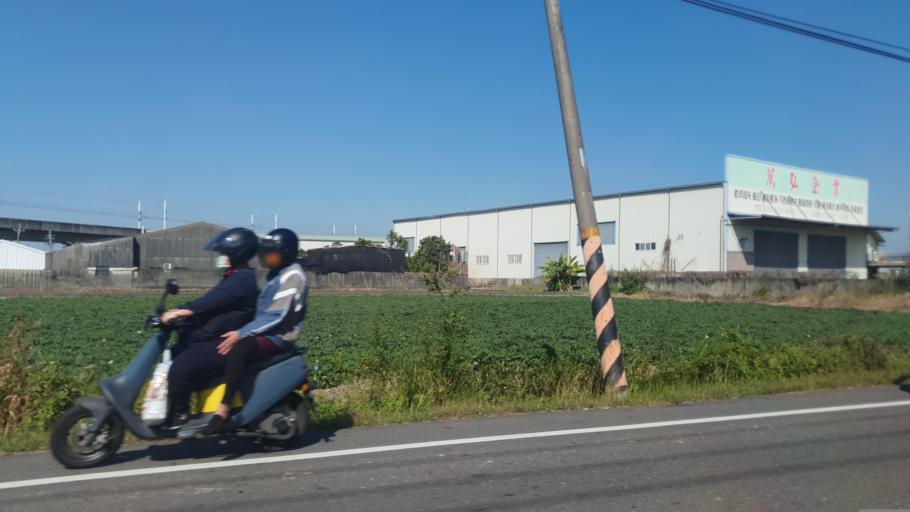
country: TW
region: Taiwan
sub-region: Tainan
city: Tainan
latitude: 23.0254
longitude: 120.2910
